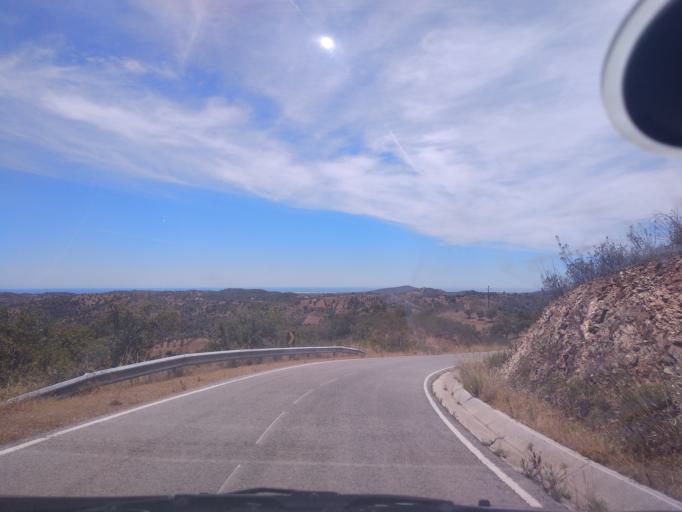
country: PT
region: Faro
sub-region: Sao Bras de Alportel
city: Sao Bras de Alportel
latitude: 37.1889
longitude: -7.7972
